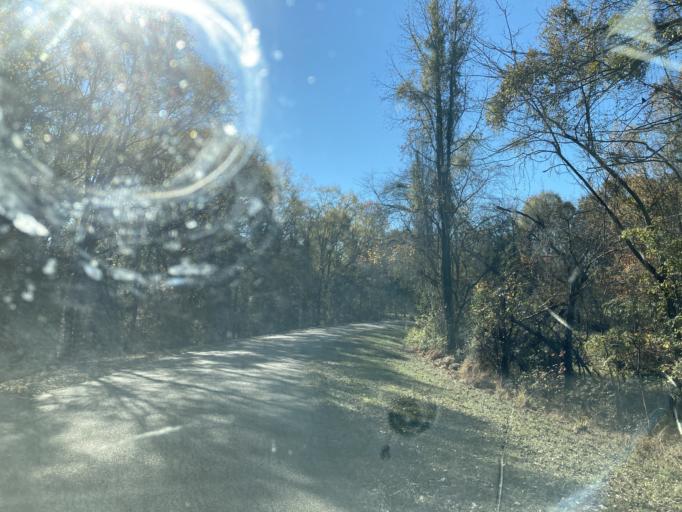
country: US
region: Mississippi
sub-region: Hinds County
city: Lynchburg
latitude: 32.5974
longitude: -90.4942
